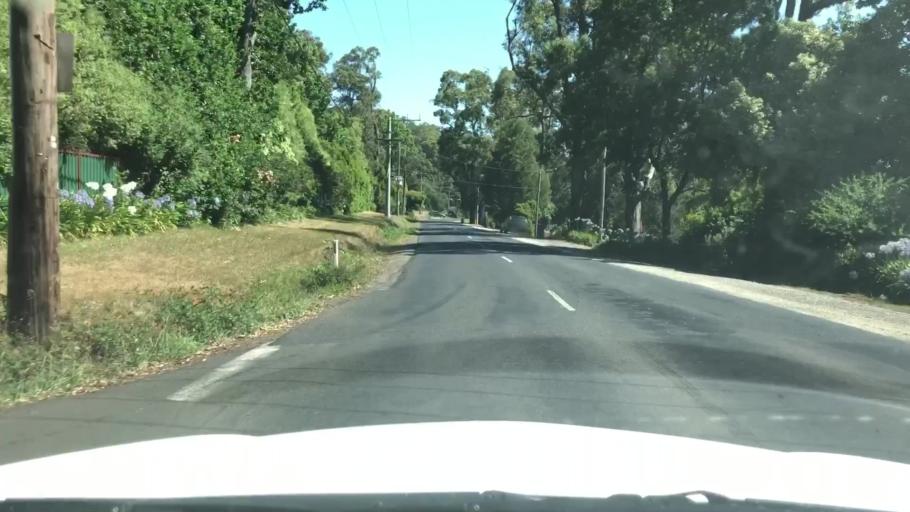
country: AU
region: Victoria
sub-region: Cardinia
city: Cockatoo
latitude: -37.9173
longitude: 145.4699
